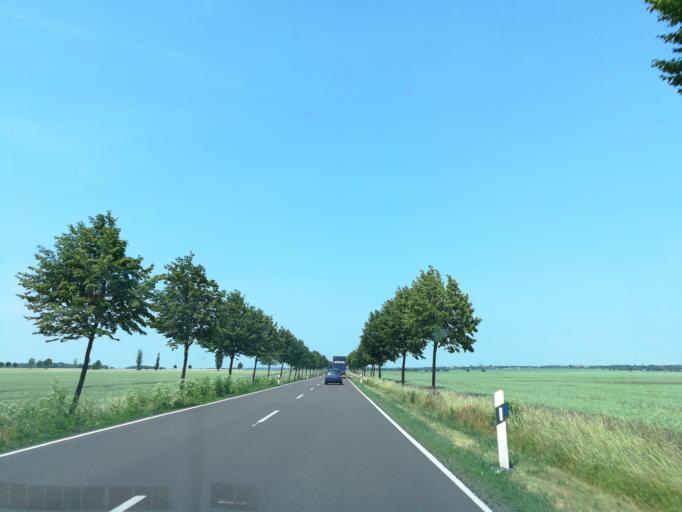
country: DE
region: Saxony-Anhalt
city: Schneidlingen
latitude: 51.9056
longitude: 11.4348
